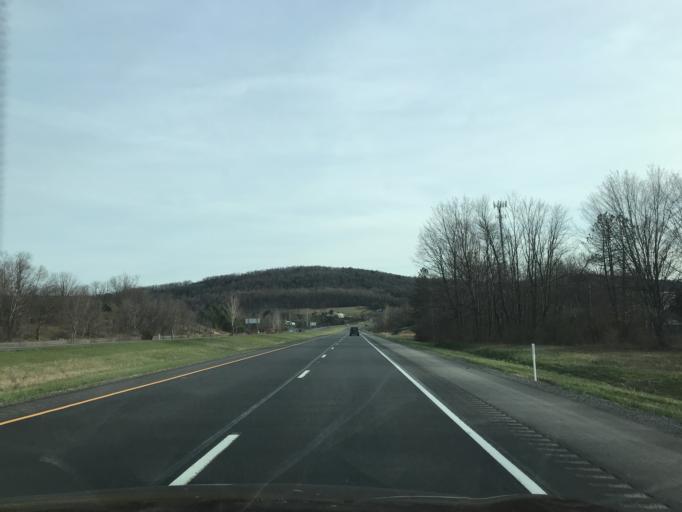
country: US
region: Pennsylvania
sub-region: Lycoming County
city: Muncy
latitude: 41.1996
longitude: -76.7694
